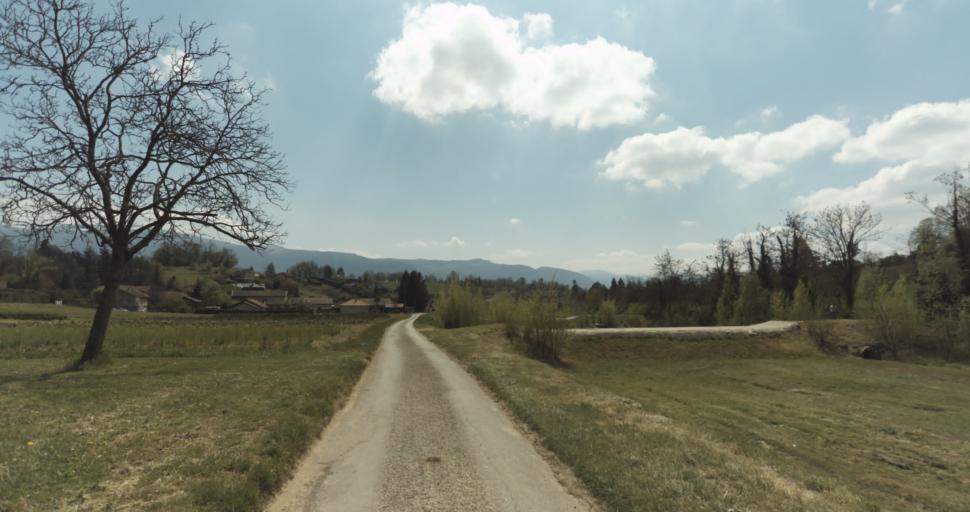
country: FR
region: Rhone-Alpes
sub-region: Departement de l'Isere
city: Saint-Marcellin
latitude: 45.1643
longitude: 5.3188
